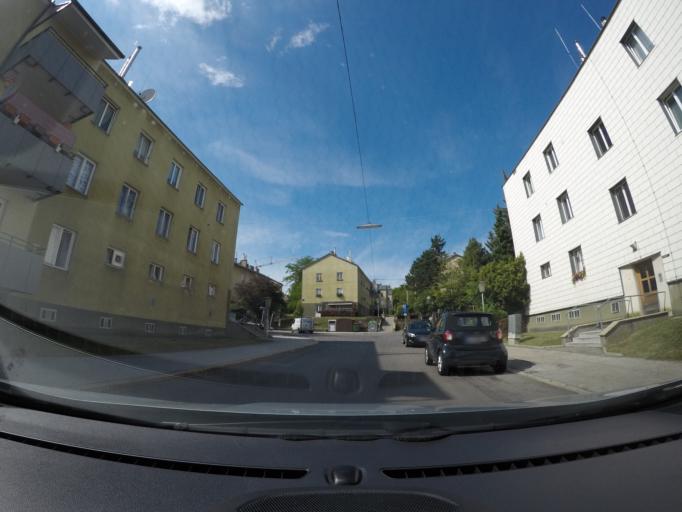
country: AT
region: Lower Austria
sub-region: Politischer Bezirk Modling
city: Perchtoldsdorf
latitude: 48.2034
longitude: 16.2749
